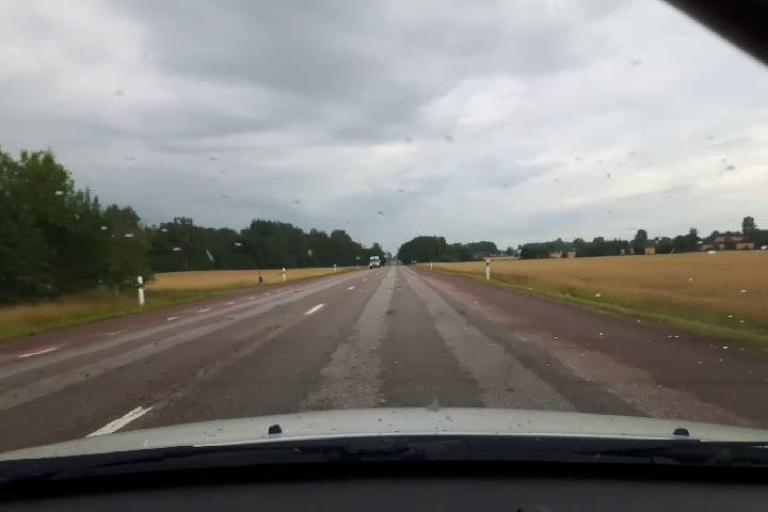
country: SE
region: Uppsala
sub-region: Osthammars Kommun
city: Bjorklinge
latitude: 59.9607
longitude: 17.5833
